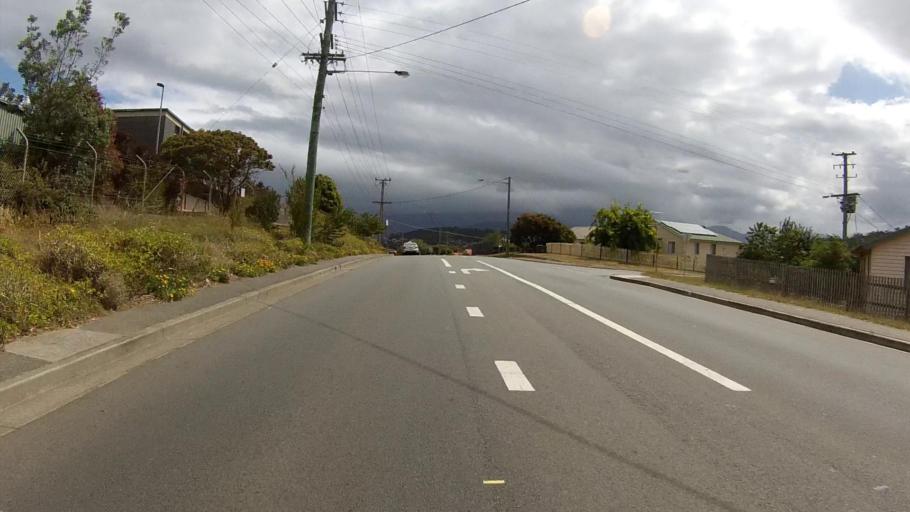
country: AU
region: Tasmania
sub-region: Clarence
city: Warrane
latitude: -42.8639
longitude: 147.3767
